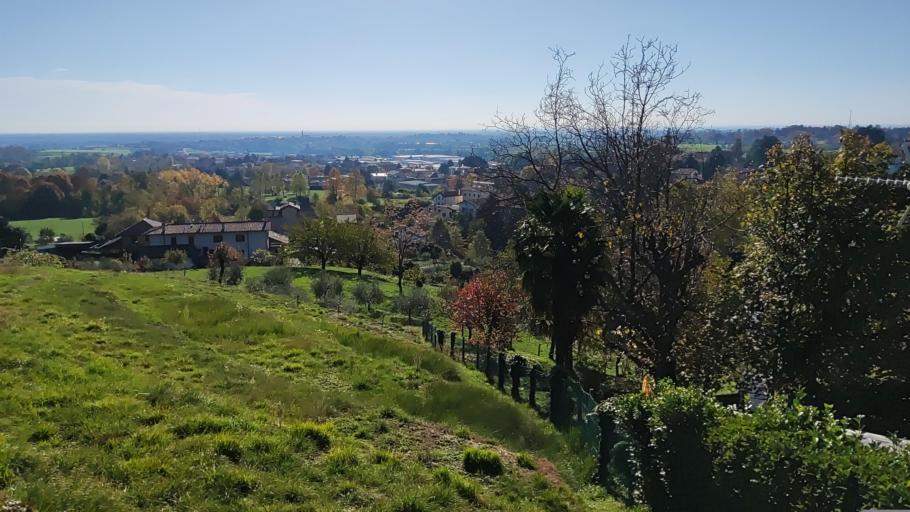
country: IT
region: Lombardy
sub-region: Provincia di Lecco
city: Missaglia
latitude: 45.7147
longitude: 9.3366
